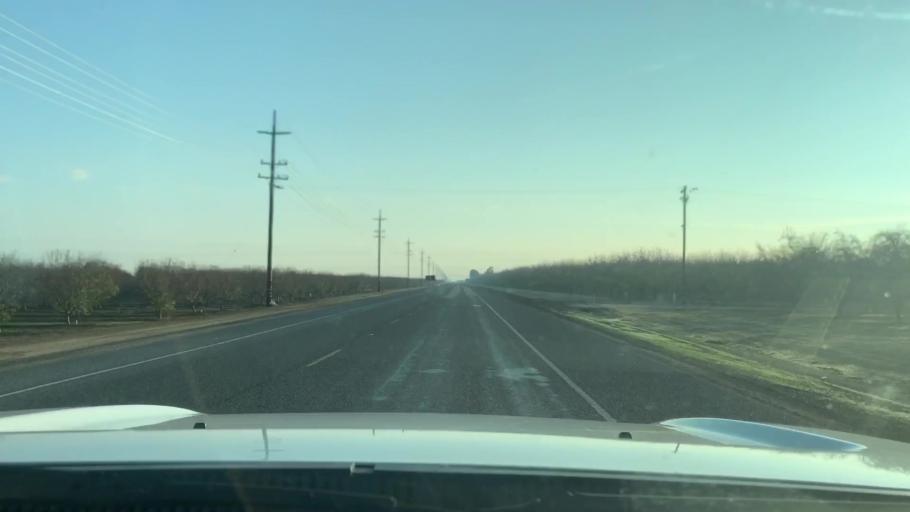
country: US
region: California
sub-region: Kern County
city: Wasco
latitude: 35.6014
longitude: -119.4343
